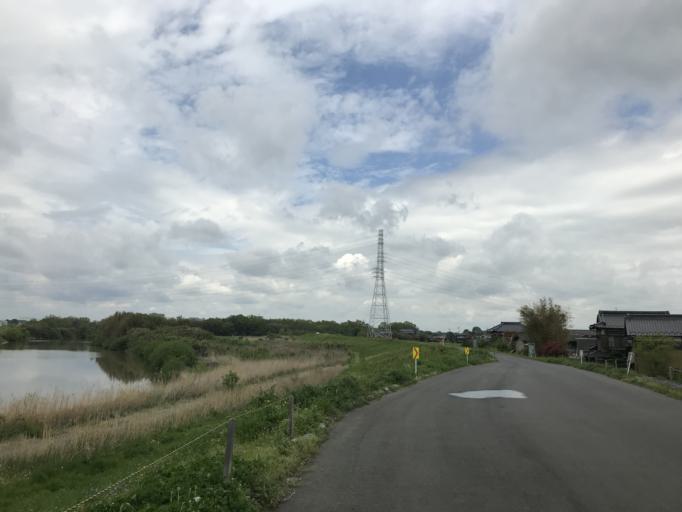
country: JP
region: Ibaraki
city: Mitsukaido
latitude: 36.0070
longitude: 139.9963
